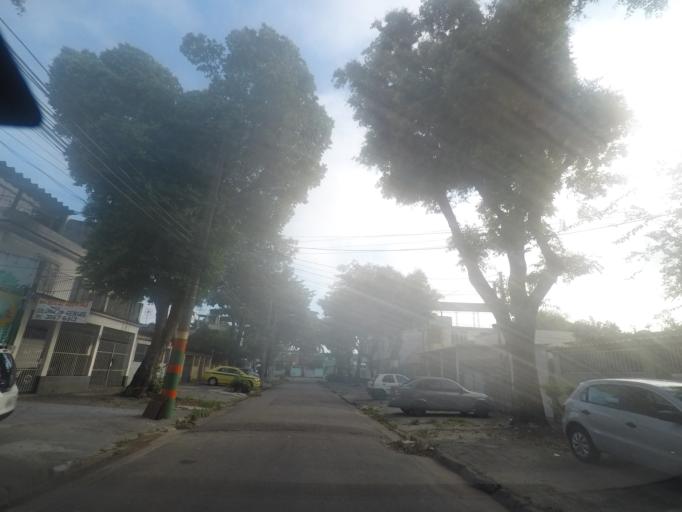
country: BR
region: Rio de Janeiro
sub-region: Duque De Caxias
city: Duque de Caxias
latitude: -22.8355
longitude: -43.2704
